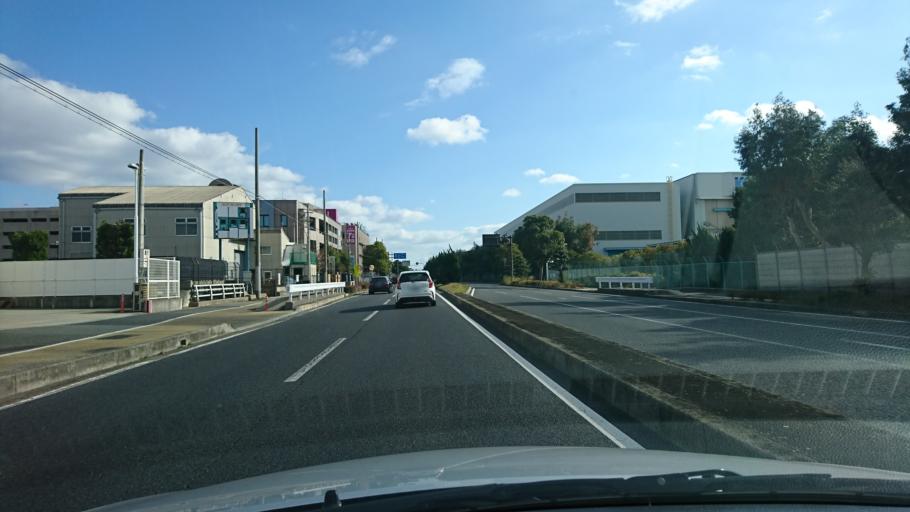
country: JP
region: Hyogo
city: Akashi
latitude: 34.6794
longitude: 134.9325
